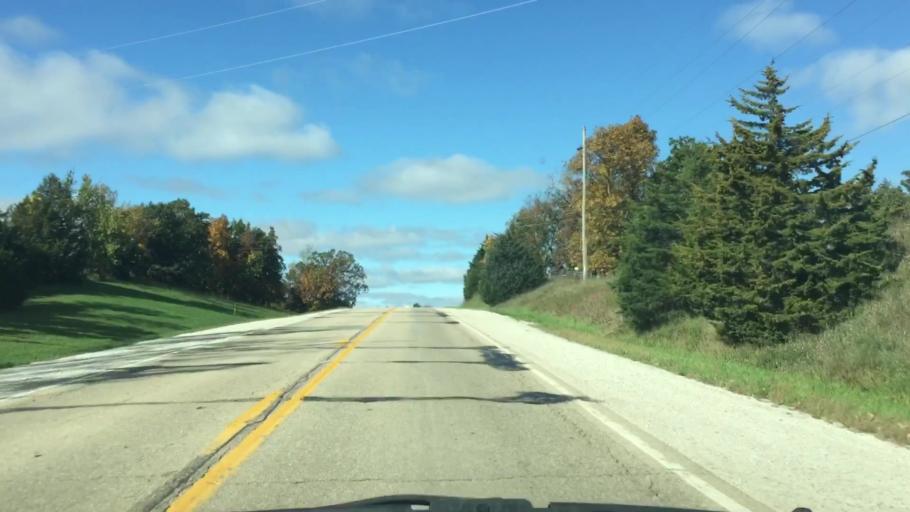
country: US
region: Iowa
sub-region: Decatur County
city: Leon
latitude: 40.7416
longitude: -93.7936
